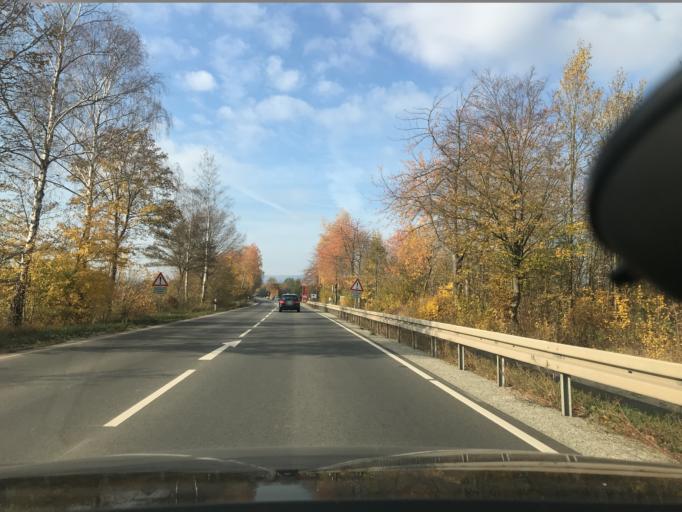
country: DE
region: Hesse
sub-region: Regierungsbezirk Kassel
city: Eschwege
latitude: 51.1983
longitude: 10.0675
